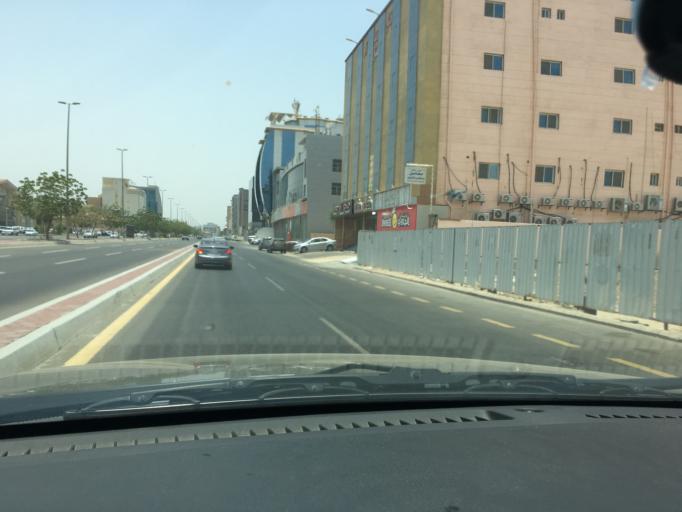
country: SA
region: Makkah
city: Jeddah
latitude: 21.6307
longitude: 39.1339
